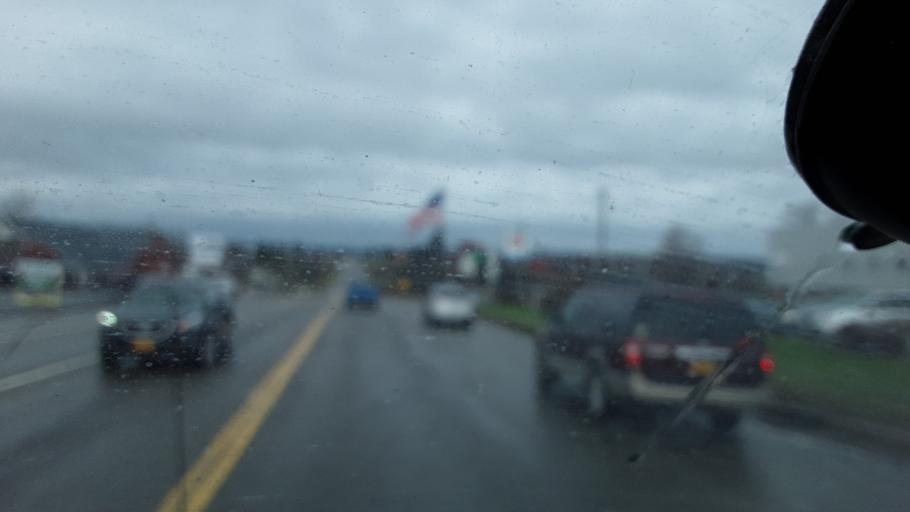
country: US
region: New York
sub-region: Cattaraugus County
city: Yorkshire
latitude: 42.5302
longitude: -78.4785
